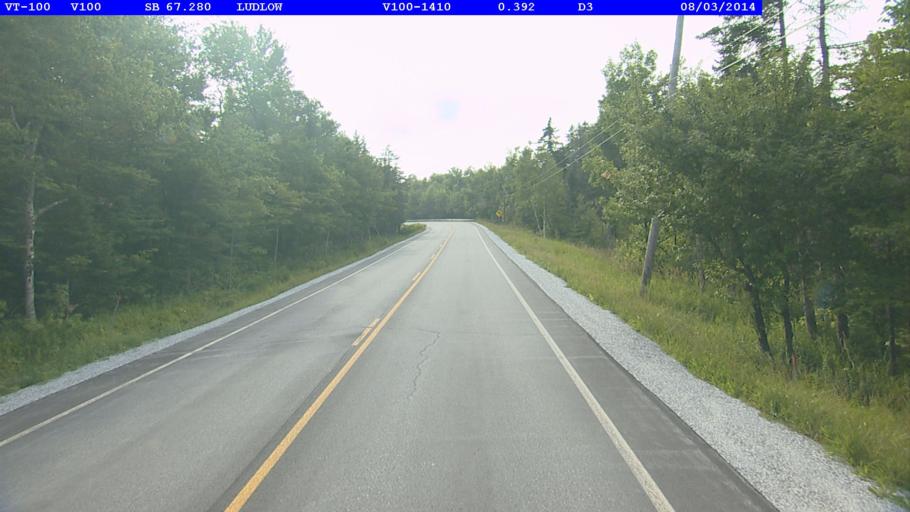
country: US
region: Vermont
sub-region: Windsor County
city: Chester
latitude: 43.3548
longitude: -72.7505
